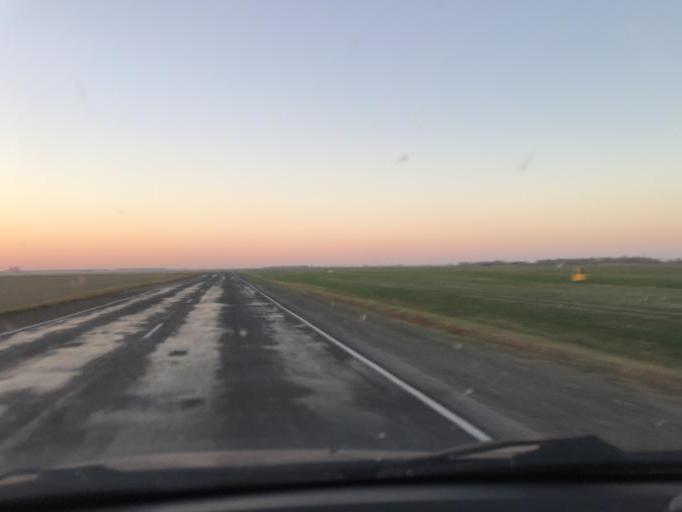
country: BY
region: Gomel
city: Horad Rechytsa
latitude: 52.1634
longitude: 30.5841
